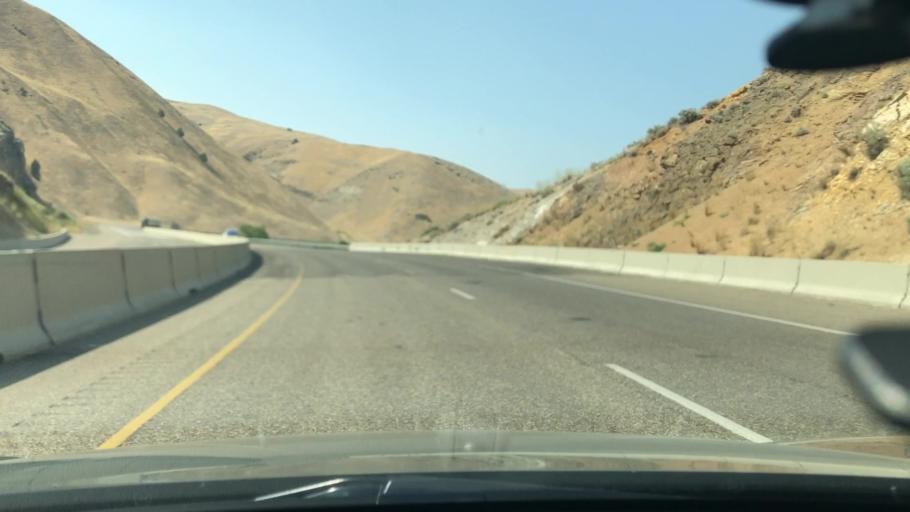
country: US
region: Idaho
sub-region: Washington County
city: Weiser
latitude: 44.4021
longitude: -117.3090
